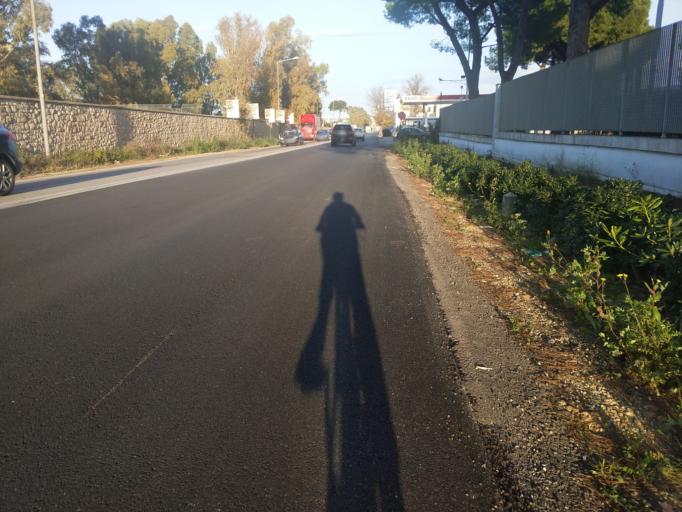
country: IT
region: Apulia
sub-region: Provincia di Bari
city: Bari
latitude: 41.1109
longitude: 16.8278
